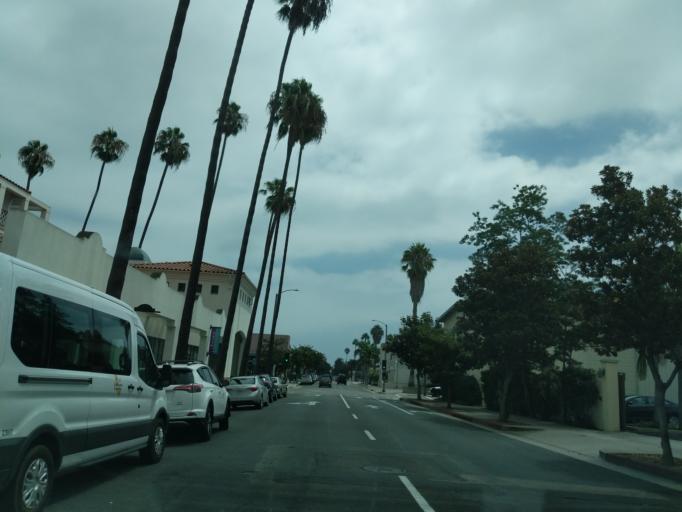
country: US
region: California
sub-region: Santa Barbara County
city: Santa Barbara
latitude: 34.4192
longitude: -119.6962
